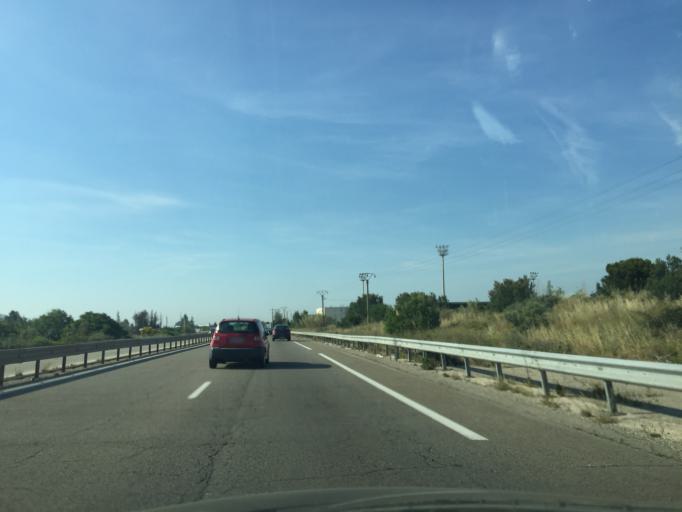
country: FR
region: Provence-Alpes-Cote d'Azur
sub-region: Departement des Bouches-du-Rhone
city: Fos-sur-Mer
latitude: 43.4413
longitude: 4.9402
